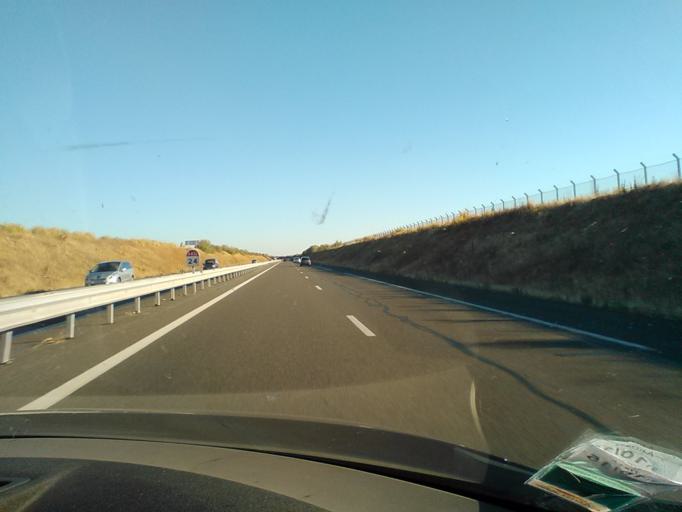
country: FR
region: Rhone-Alpes
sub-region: Departement de l'Isere
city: Janneyrias
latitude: 45.7383
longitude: 5.0957
